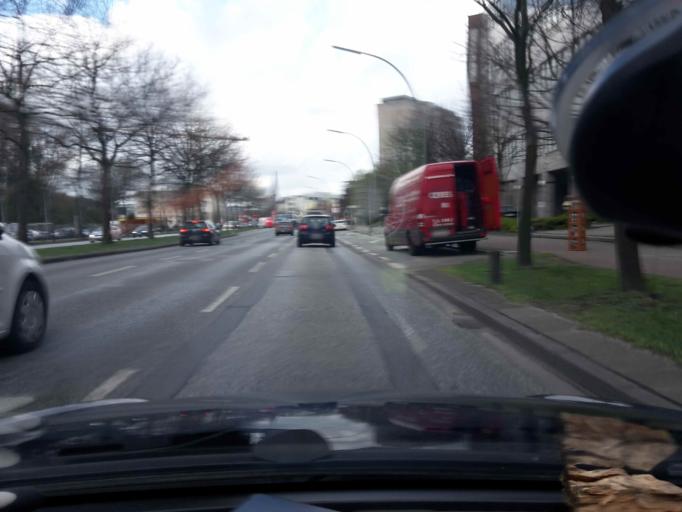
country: DE
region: Hamburg
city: Hamburg-Mitte
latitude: 53.5446
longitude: 10.0191
